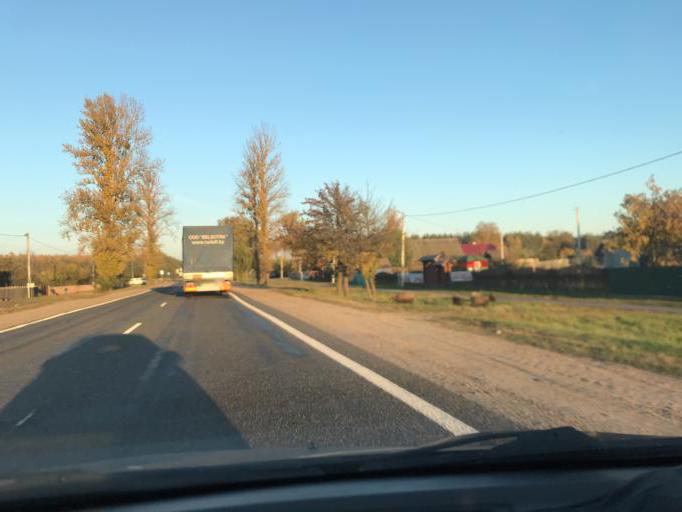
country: BY
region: Minsk
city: Staryya Darohi
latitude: 53.0416
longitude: 28.3259
